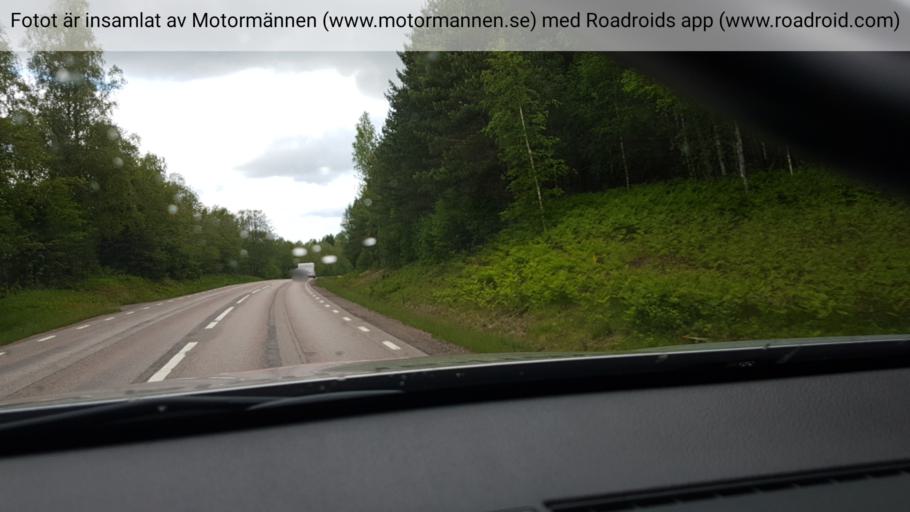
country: SE
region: Vaermland
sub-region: Hagfors Kommun
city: Ekshaerad
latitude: 60.3693
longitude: 13.3053
